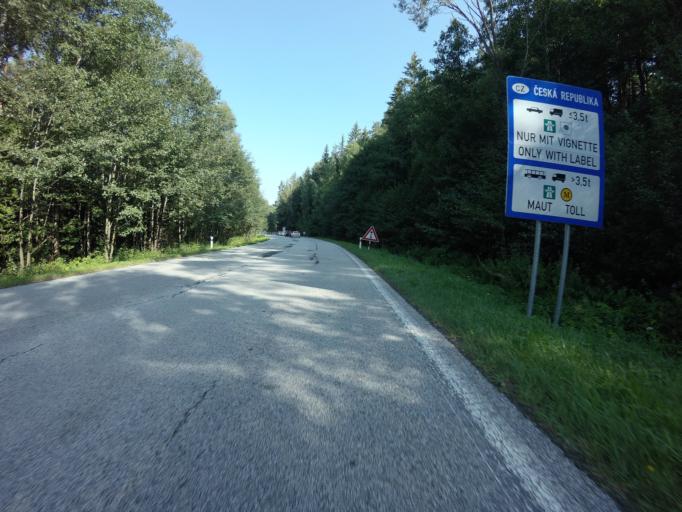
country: CZ
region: Jihocesky
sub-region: Okres Cesky Krumlov
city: Vyssi Brod
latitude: 48.5745
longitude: 14.3215
